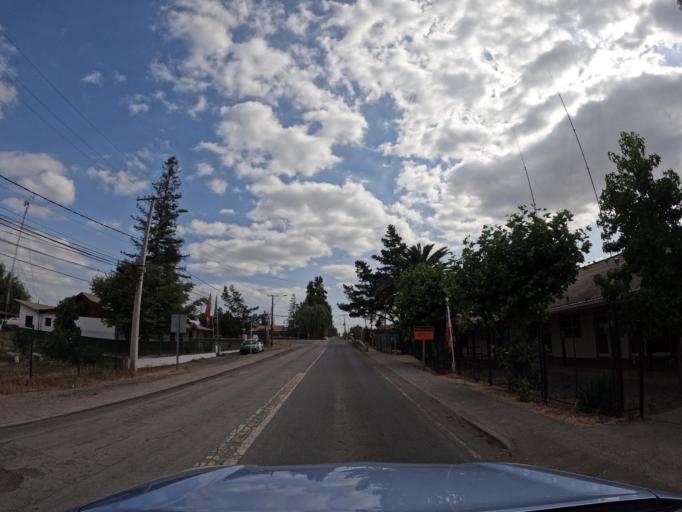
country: CL
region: Maule
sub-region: Provincia de Curico
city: Molina
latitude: -35.1616
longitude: -71.2871
